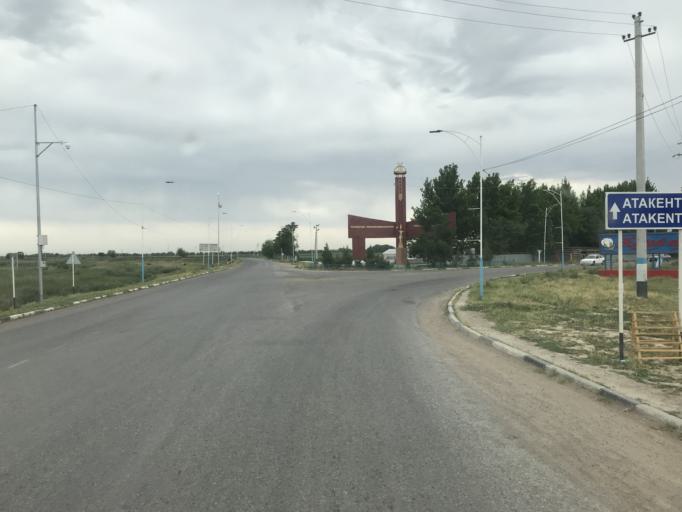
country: KZ
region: Ongtustik Qazaqstan
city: Ilyich
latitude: 40.9570
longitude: 68.4639
